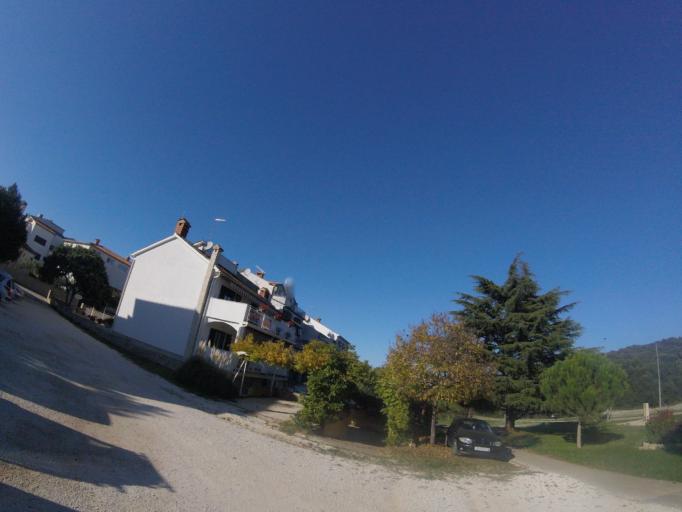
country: HR
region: Istarska
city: Vrsar
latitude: 45.1535
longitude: 13.6112
